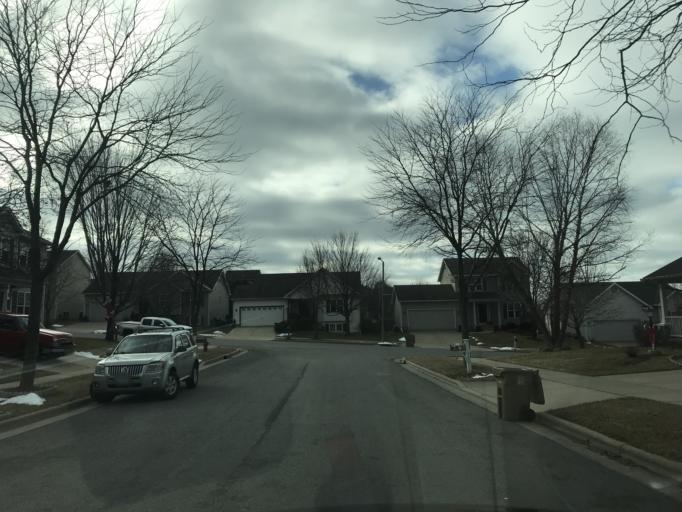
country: US
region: Wisconsin
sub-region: Dane County
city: Monona
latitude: 43.1124
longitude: -89.2890
